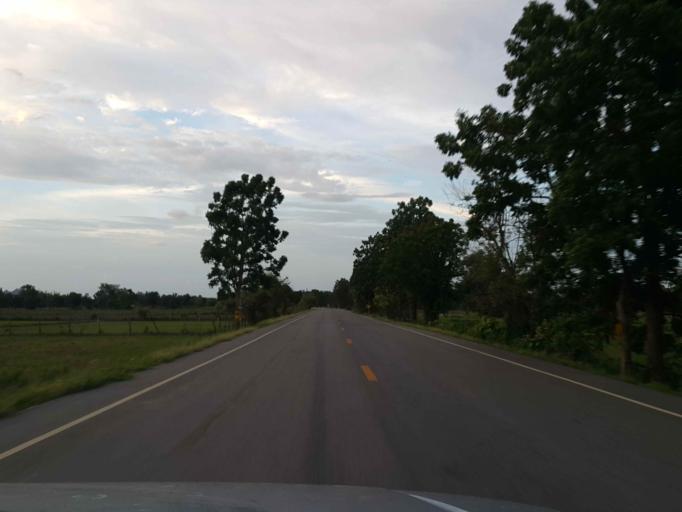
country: TH
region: Sukhothai
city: Ban Dan Lan Hoi
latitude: 17.0778
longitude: 99.5903
